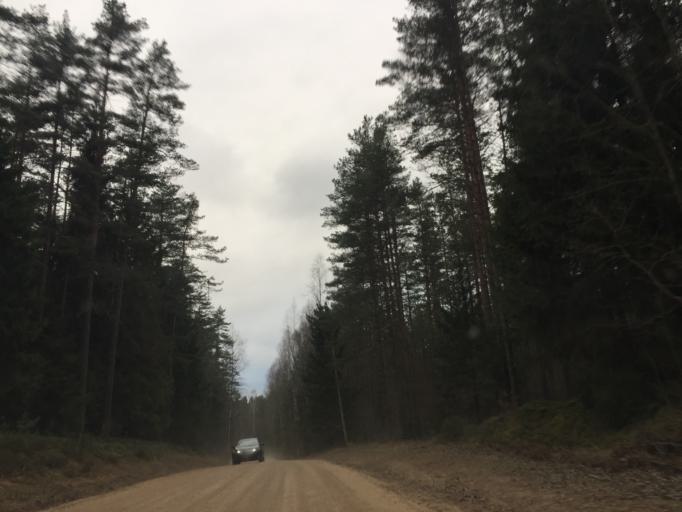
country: LV
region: Cesu Rajons
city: Cesis
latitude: 57.3403
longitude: 25.2623
